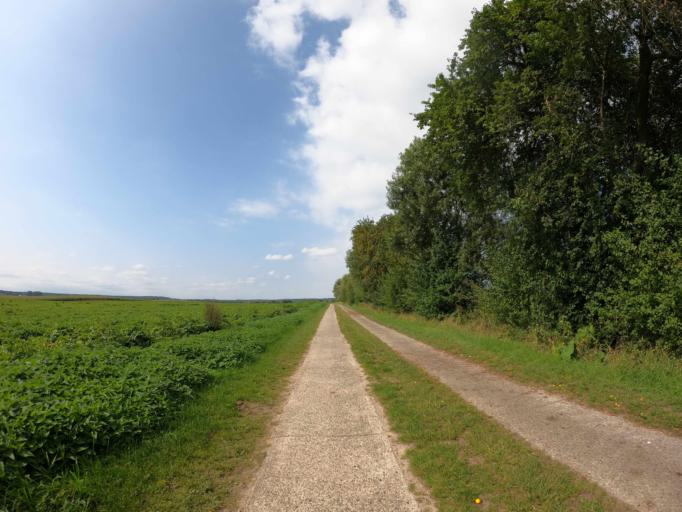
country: DE
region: Mecklenburg-Vorpommern
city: Malchow
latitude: 53.4358
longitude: 12.4932
